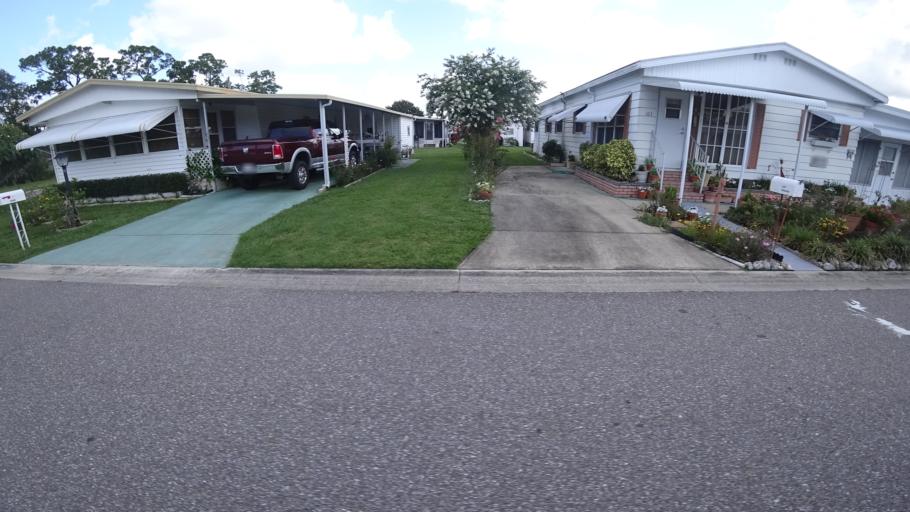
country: US
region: Florida
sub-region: Manatee County
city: West Samoset
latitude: 27.4482
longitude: -82.5626
